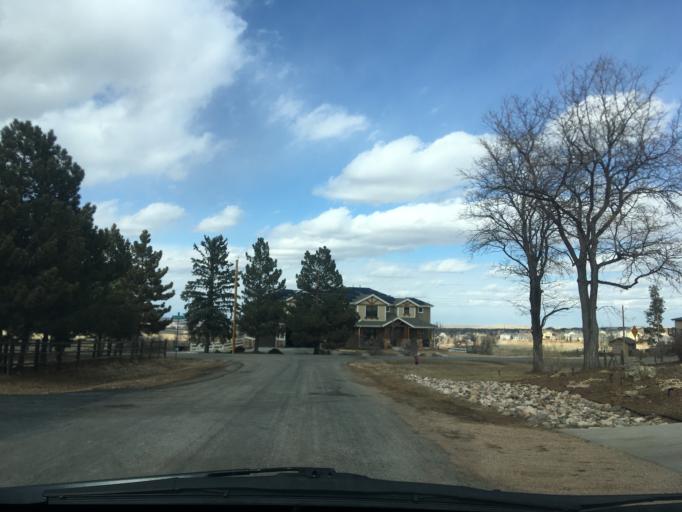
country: US
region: Colorado
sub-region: Boulder County
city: Lafayette
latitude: 39.9624
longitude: -105.0552
